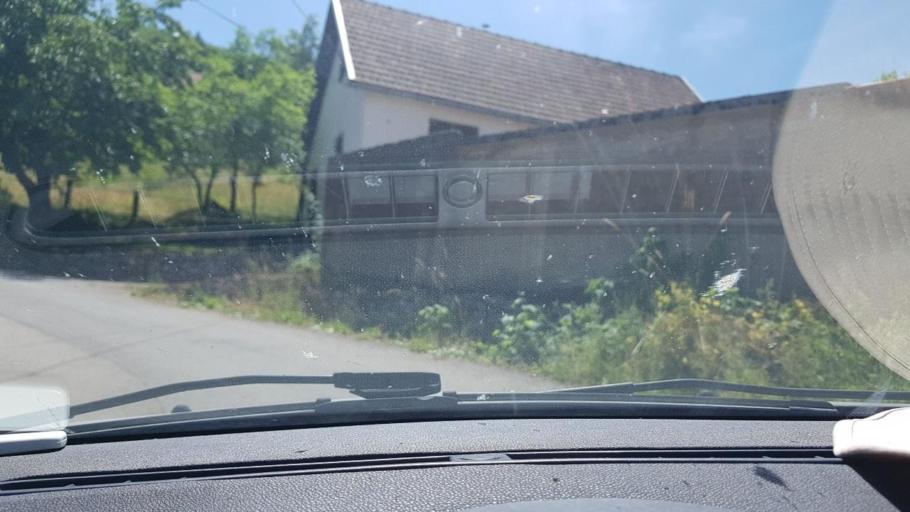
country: HR
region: Licko-Senjska
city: Otocac
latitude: 44.7866
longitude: 15.3662
